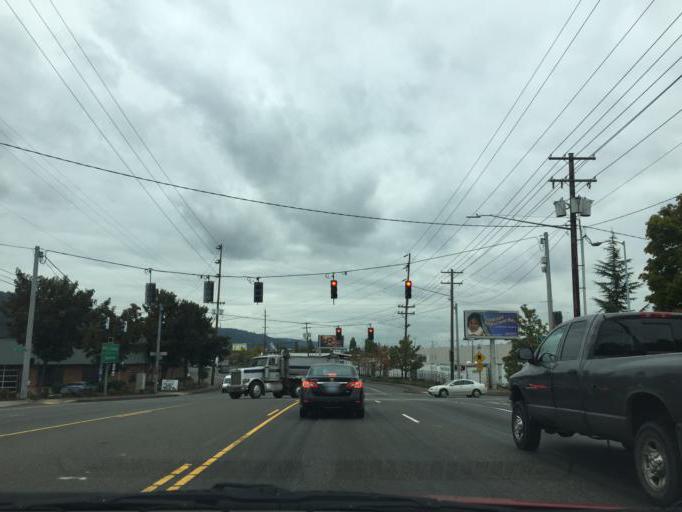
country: US
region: Oregon
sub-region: Multnomah County
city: Portland
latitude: 45.5436
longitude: -122.7022
